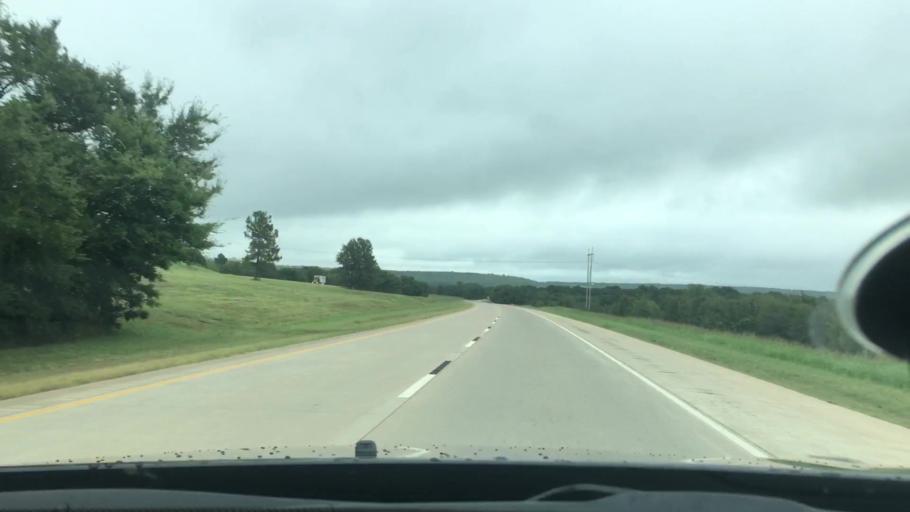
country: US
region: Oklahoma
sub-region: Okmulgee County
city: Henryetta
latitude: 35.4296
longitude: -95.8998
